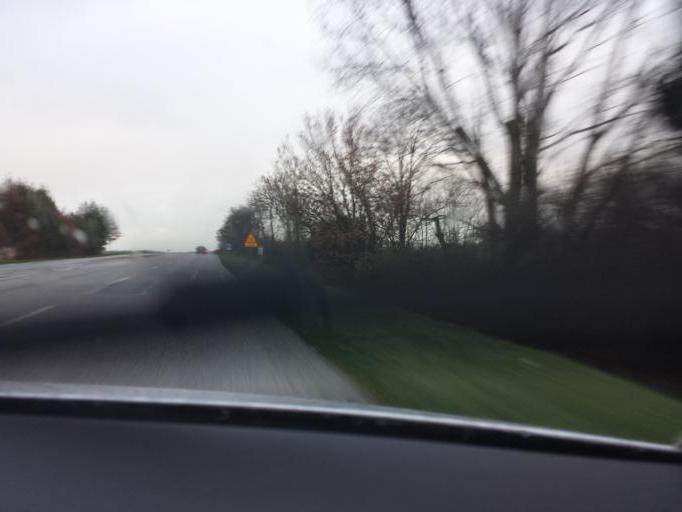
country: FR
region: Haute-Normandie
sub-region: Departement de l'Eure
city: Breuilpont
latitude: 49.0139
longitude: 1.4466
